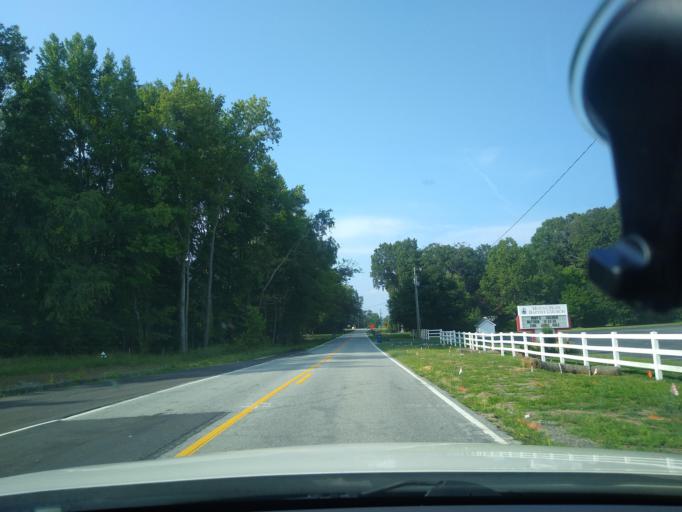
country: US
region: North Carolina
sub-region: Guilford County
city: McLeansville
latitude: 36.0879
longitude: -79.6797
